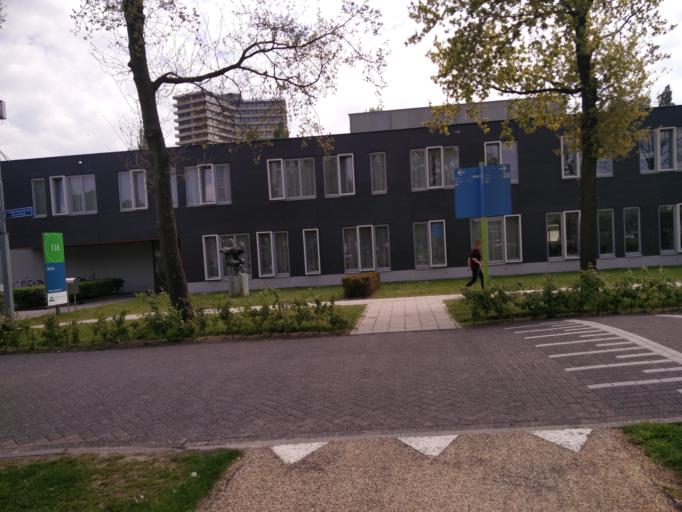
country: NL
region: Gelderland
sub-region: Gemeente Wageningen
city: Wageningen
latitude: 51.9831
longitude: 5.6614
